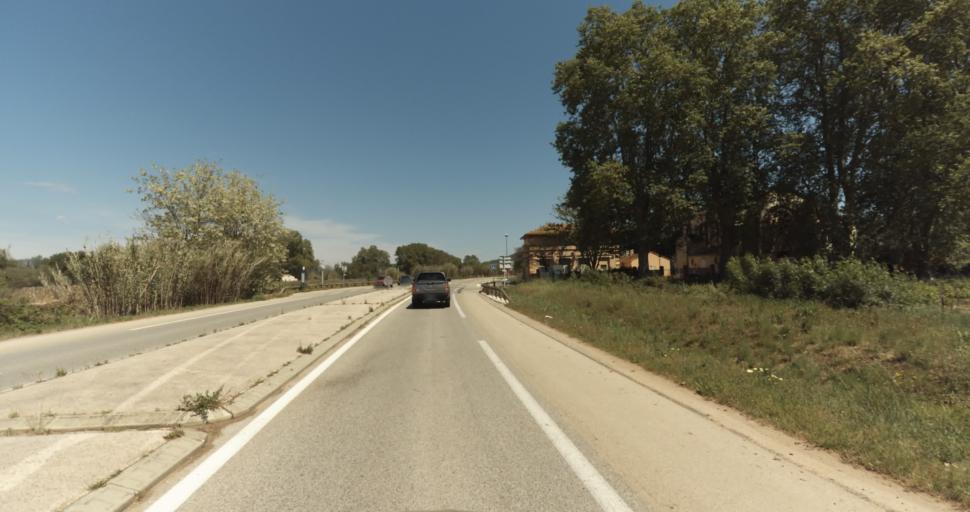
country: FR
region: Provence-Alpes-Cote d'Azur
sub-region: Departement du Var
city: Pierrefeu-du-Var
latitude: 43.1901
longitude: 6.1237
